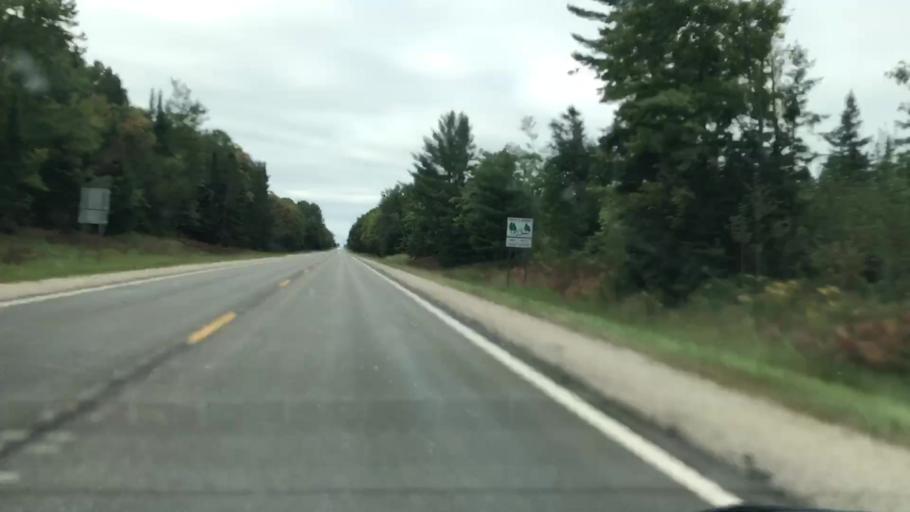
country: US
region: Michigan
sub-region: Luce County
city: Newberry
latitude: 46.2314
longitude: -85.5721
